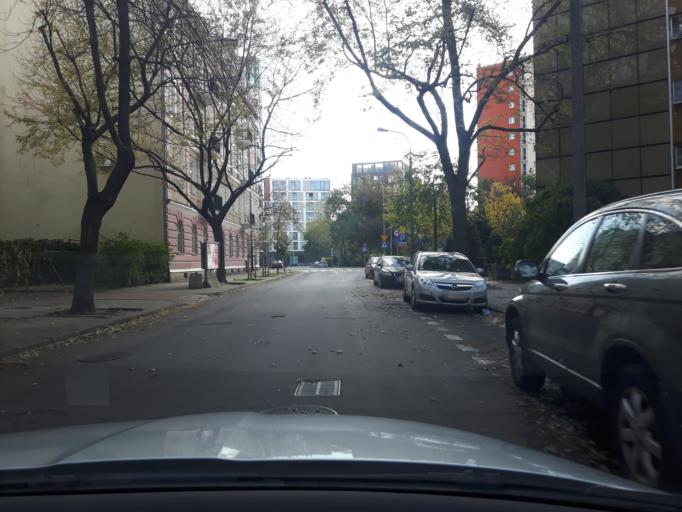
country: PL
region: Masovian Voivodeship
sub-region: Warszawa
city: Praga Polnoc
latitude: 52.2497
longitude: 21.0283
